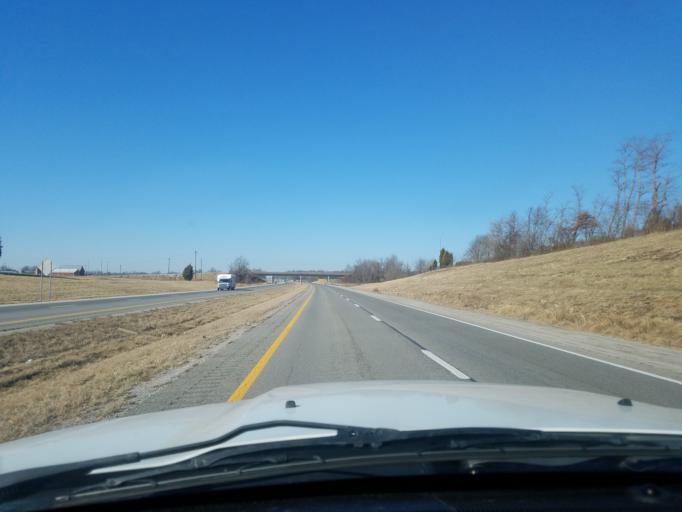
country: US
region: Kentucky
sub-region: Daviess County
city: Masonville
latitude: 37.7153
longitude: -87.0495
